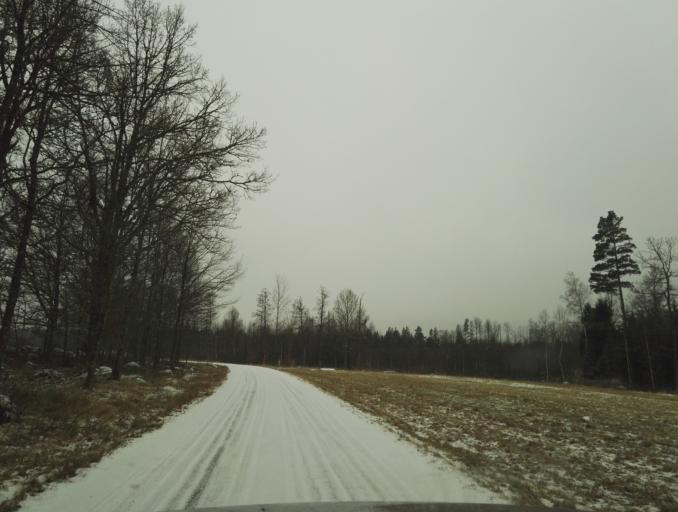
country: SE
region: Kronoberg
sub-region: Alvesta Kommun
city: Vislanda
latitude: 56.6931
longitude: 14.4190
